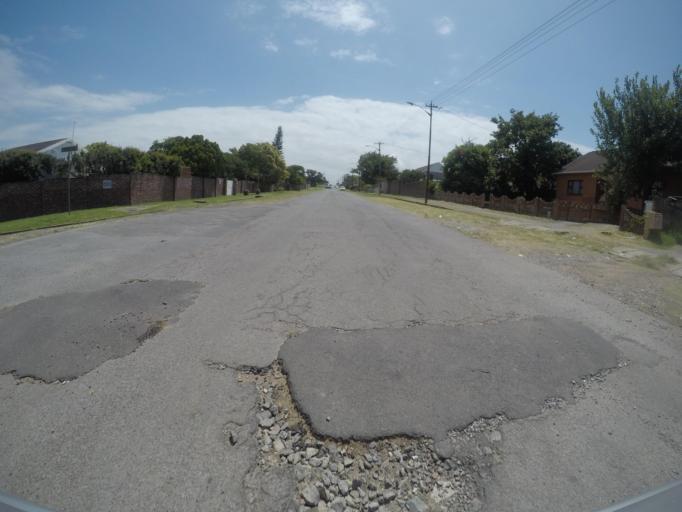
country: ZA
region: Eastern Cape
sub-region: Buffalo City Metropolitan Municipality
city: East London
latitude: -32.9744
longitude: 27.8725
